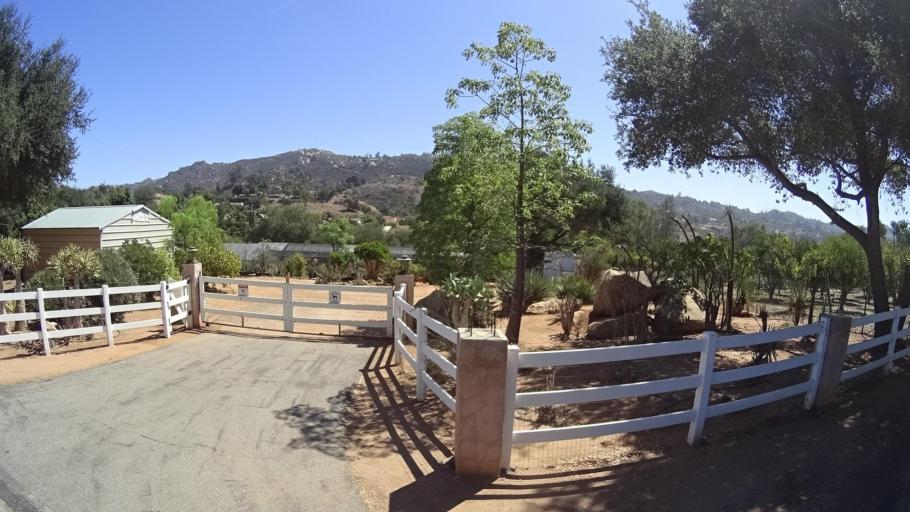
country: US
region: California
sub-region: San Diego County
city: Rainbow
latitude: 33.4063
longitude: -117.1476
